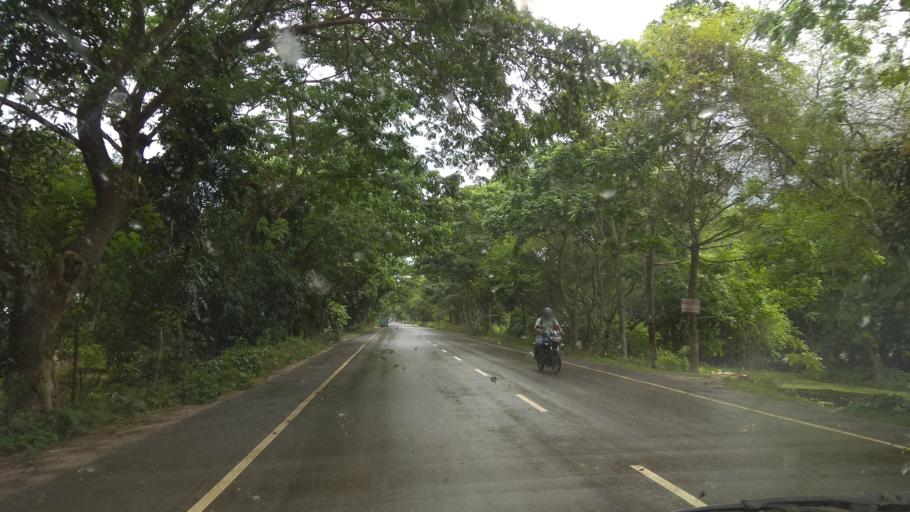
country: BD
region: Khulna
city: Kalia
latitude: 23.2465
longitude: 89.7557
